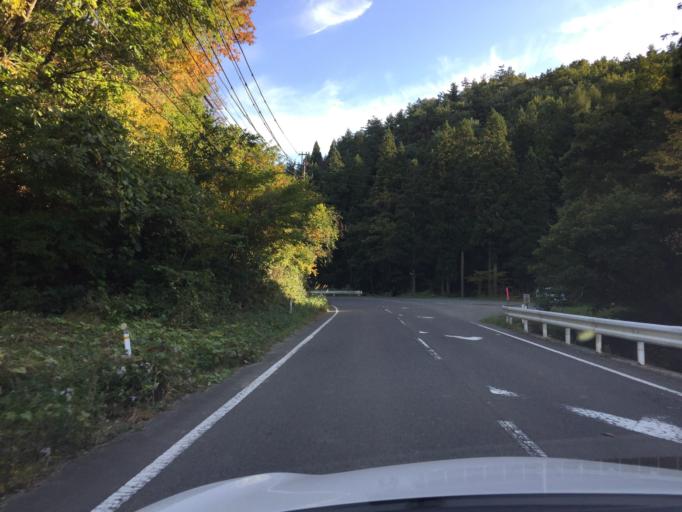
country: JP
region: Fukushima
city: Funehikimachi-funehiki
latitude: 37.3263
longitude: 140.5913
